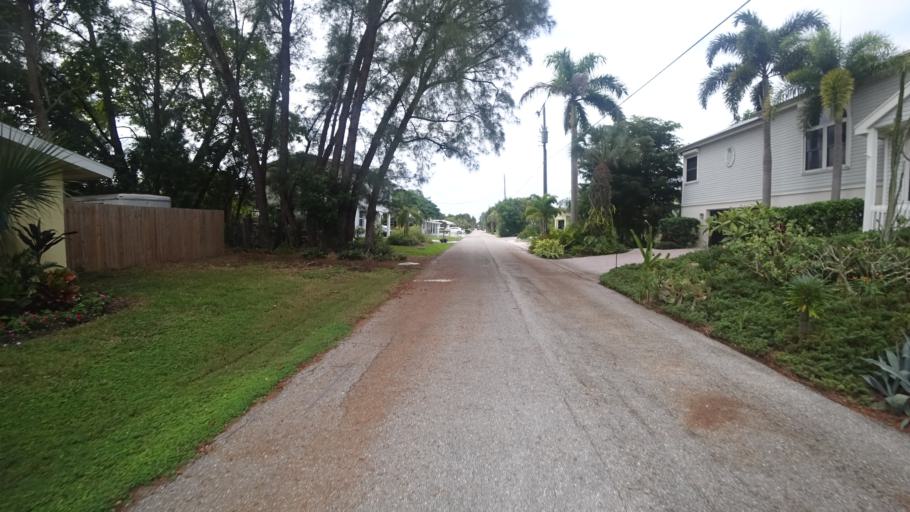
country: US
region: Florida
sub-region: Manatee County
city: Longboat Key
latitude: 27.4183
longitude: -82.6568
